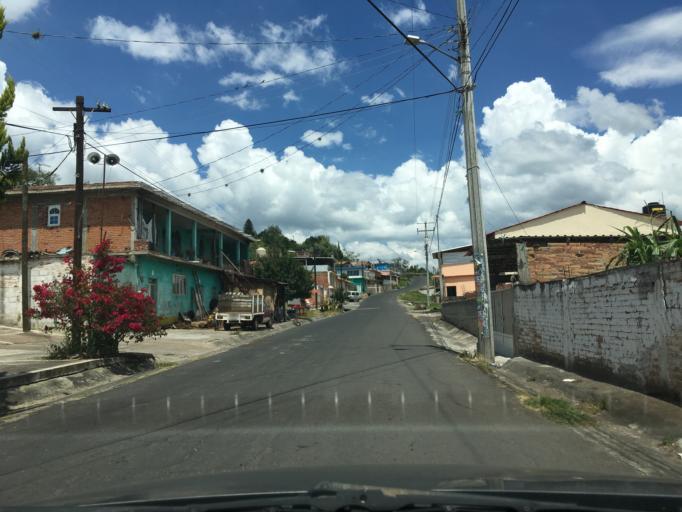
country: MX
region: Michoacan
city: Coeneo de la Libertad
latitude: 19.8438
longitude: -101.5319
